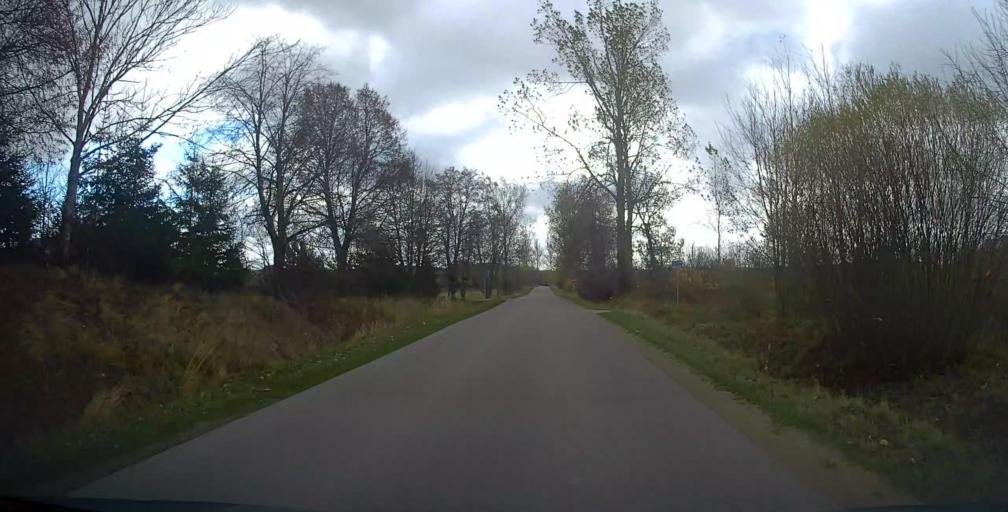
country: PL
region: Podlasie
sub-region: Suwalki
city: Suwalki
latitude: 54.3550
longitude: 22.8553
